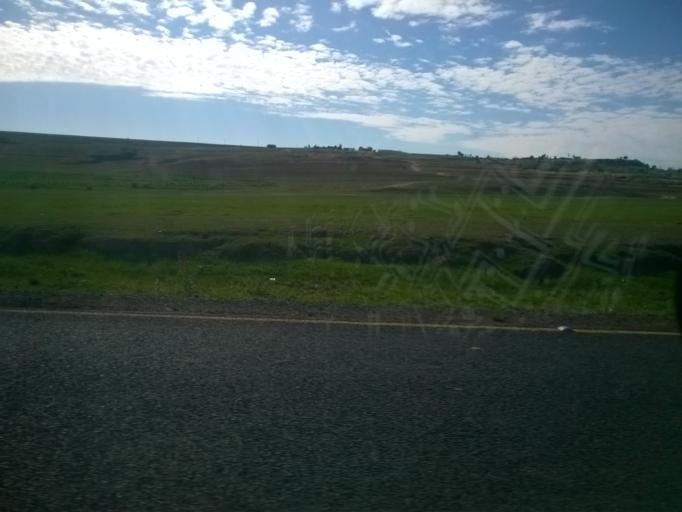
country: LS
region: Berea
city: Teyateyaneng
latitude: -29.0847
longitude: 27.8645
